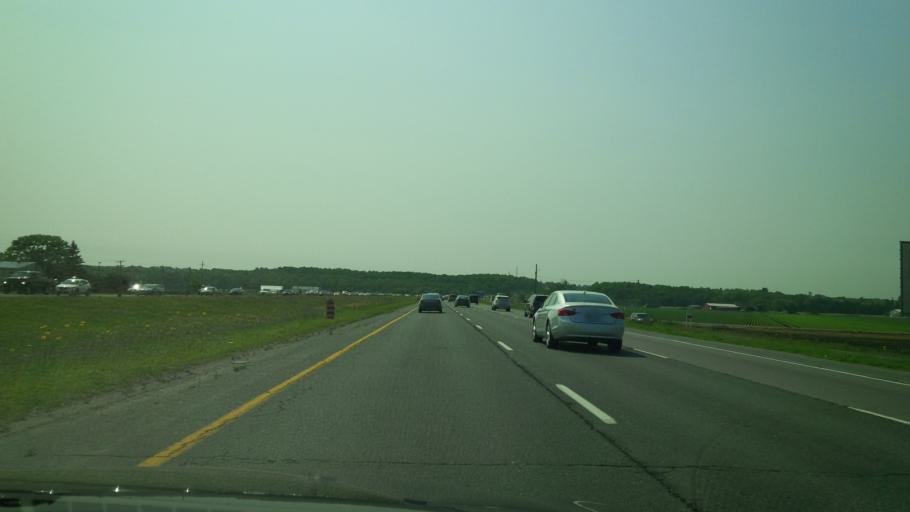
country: CA
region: Ontario
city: Bradford West Gwillimbury
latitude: 44.0431
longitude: -79.6016
